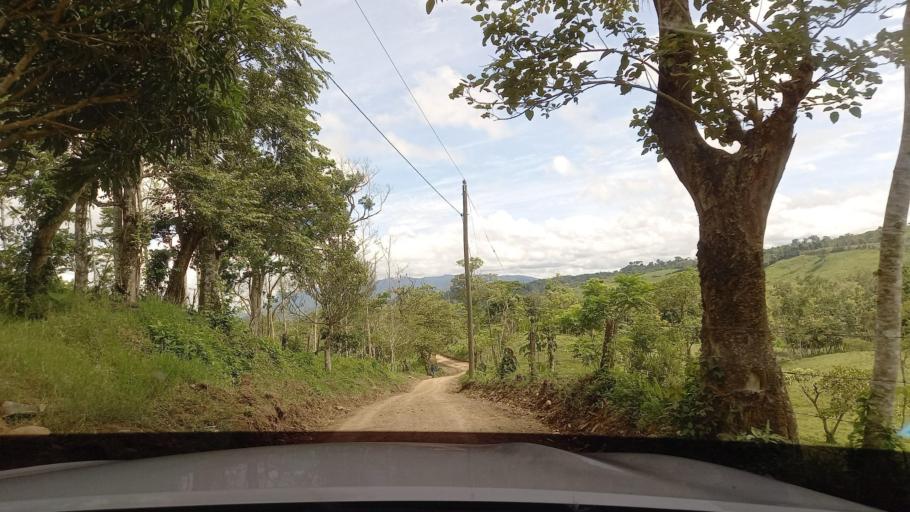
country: NI
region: Jinotega
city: San Jose de Bocay
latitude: 13.3775
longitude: -85.6852
